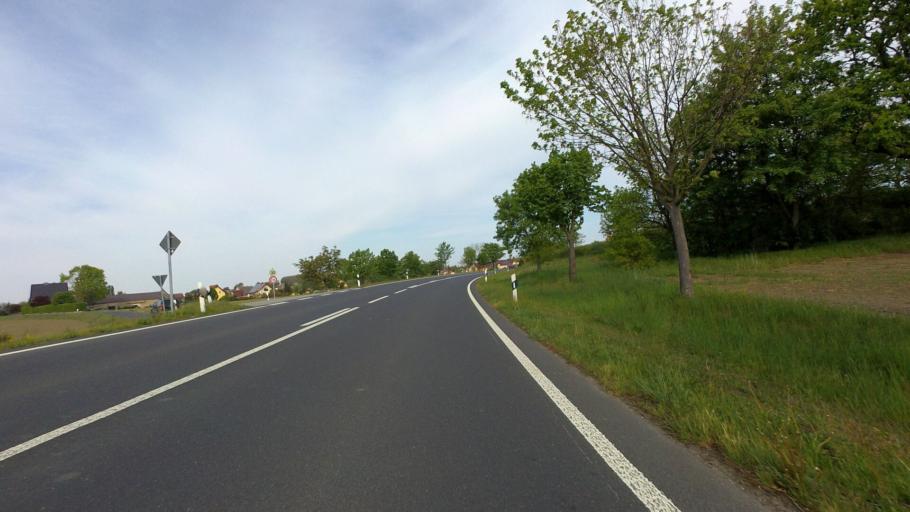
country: DE
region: Saxony
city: Tauscha
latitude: 51.2830
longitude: 13.7999
